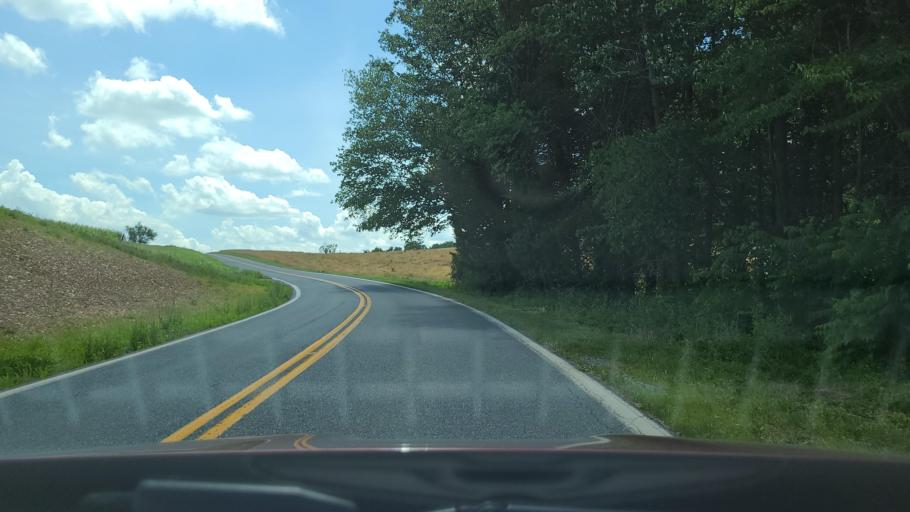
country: US
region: Maryland
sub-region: Montgomery County
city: Clarksburg
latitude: 39.2698
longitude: -77.2514
